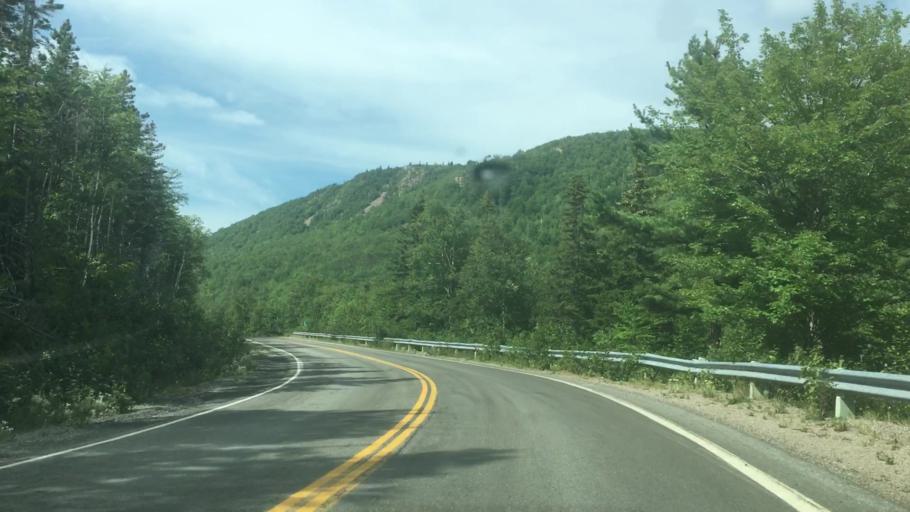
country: CA
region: Nova Scotia
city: Sydney Mines
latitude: 46.5810
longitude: -60.3915
